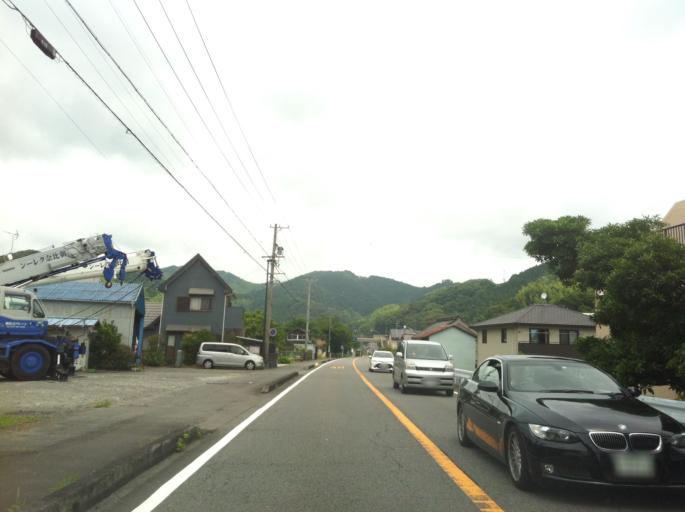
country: JP
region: Shizuoka
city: Fujieda
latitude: 34.9141
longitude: 138.2810
